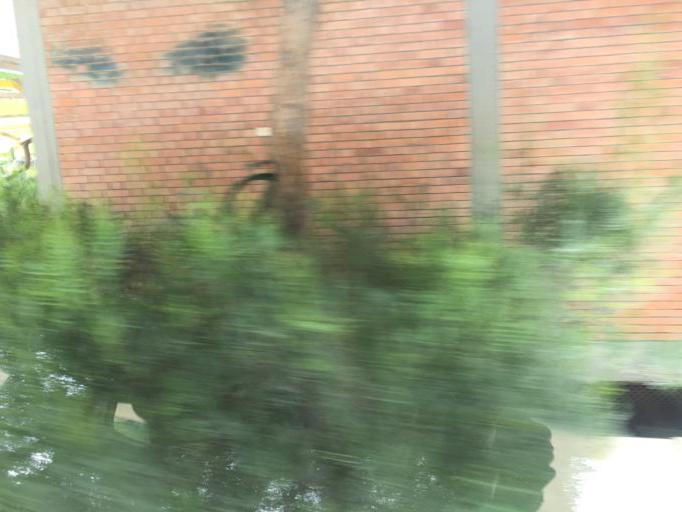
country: PE
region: Callao
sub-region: Callao
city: Callao
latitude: -12.0727
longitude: -77.0809
